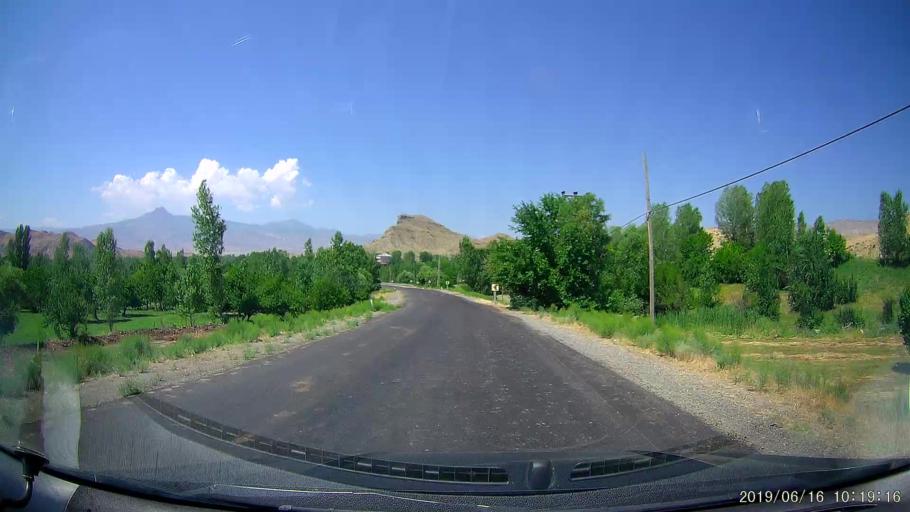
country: TR
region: Igdir
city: Tuzluca
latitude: 40.1559
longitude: 43.6581
